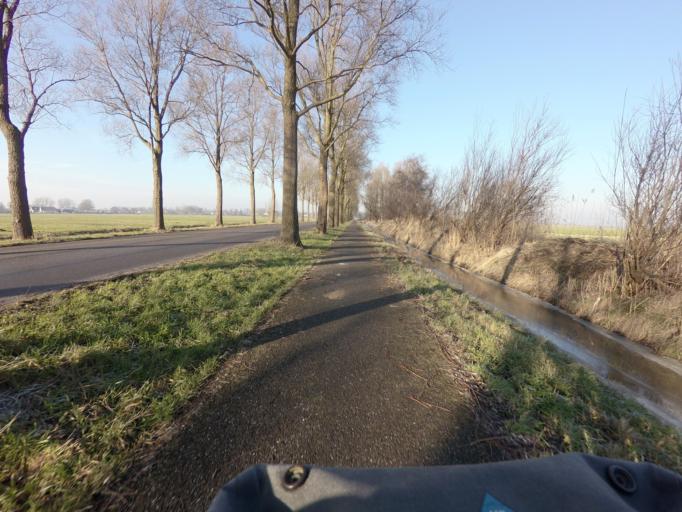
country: NL
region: North Holland
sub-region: Gemeente Amsterdam
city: Amsterdam-Zuidoost
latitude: 52.2621
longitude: 4.9855
